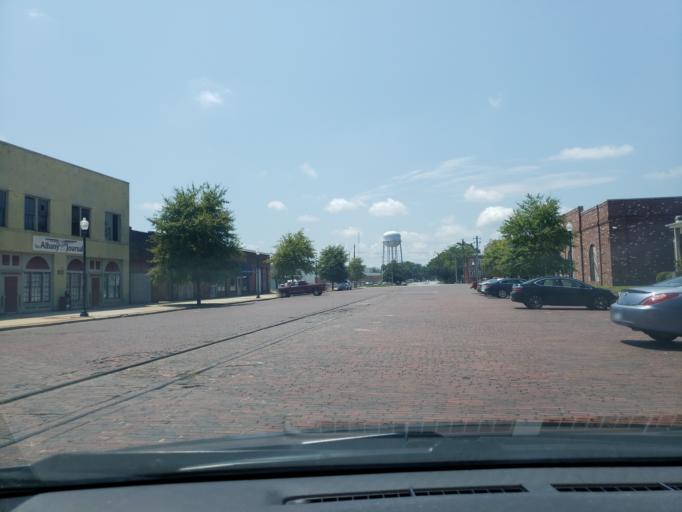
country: US
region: Georgia
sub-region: Dougherty County
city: Albany
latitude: 31.5816
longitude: -84.1498
